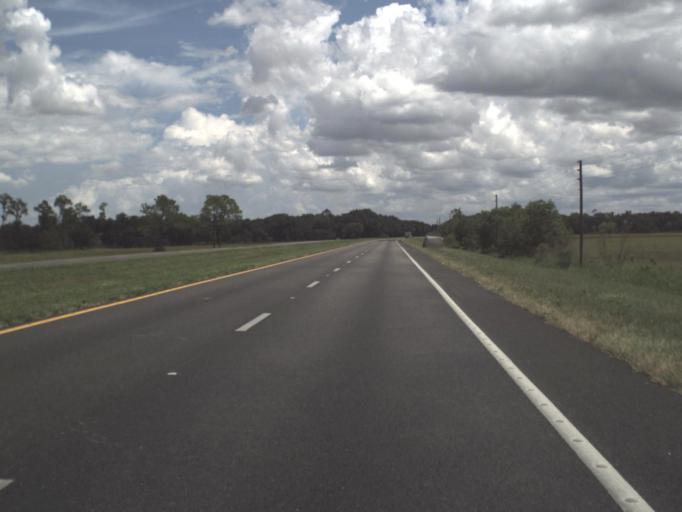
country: US
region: Florida
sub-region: Polk County
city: Alturas
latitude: 27.9116
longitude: -81.6900
